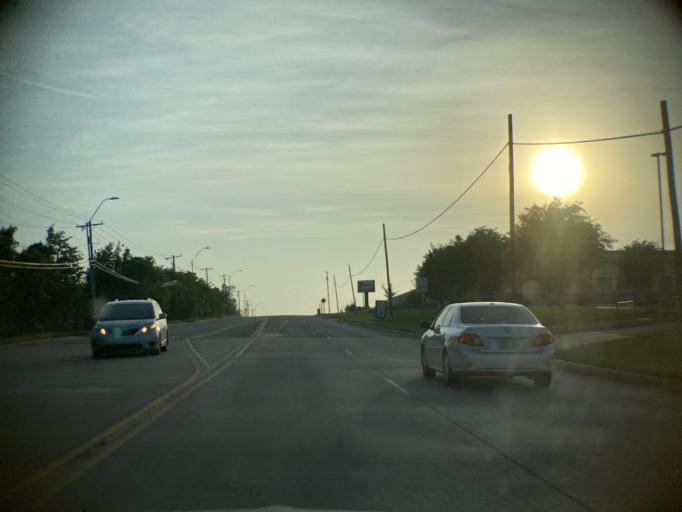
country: US
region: Oklahoma
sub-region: Oklahoma County
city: Midwest City
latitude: 35.4352
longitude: -97.3536
